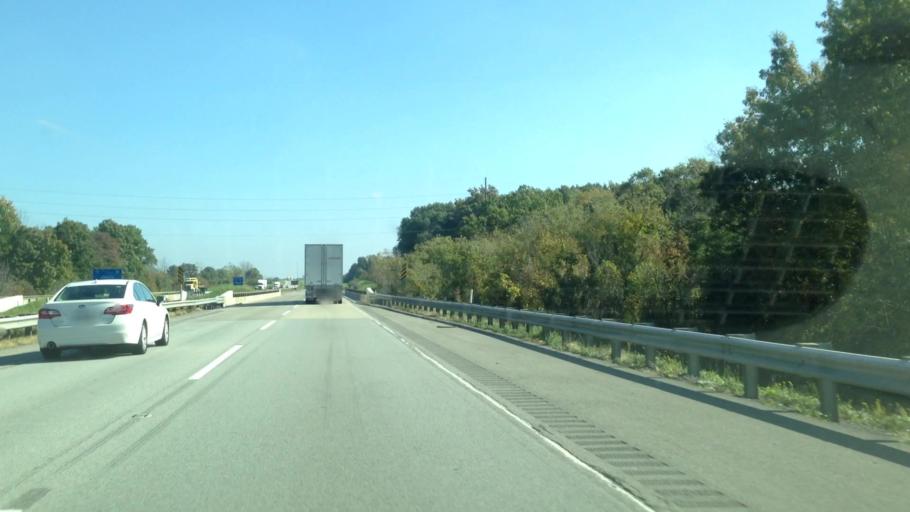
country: US
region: Indiana
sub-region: LaPorte County
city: LaPorte
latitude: 41.6588
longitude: -86.7515
